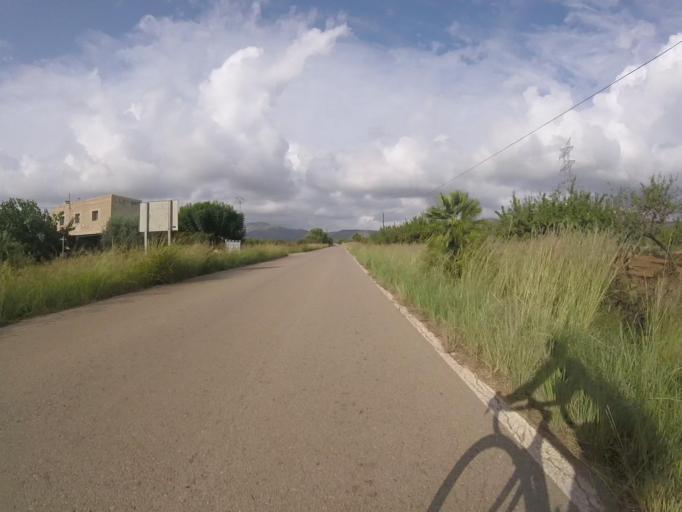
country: ES
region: Valencia
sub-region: Provincia de Castello
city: Orpesa/Oropesa del Mar
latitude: 40.1390
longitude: 0.1489
